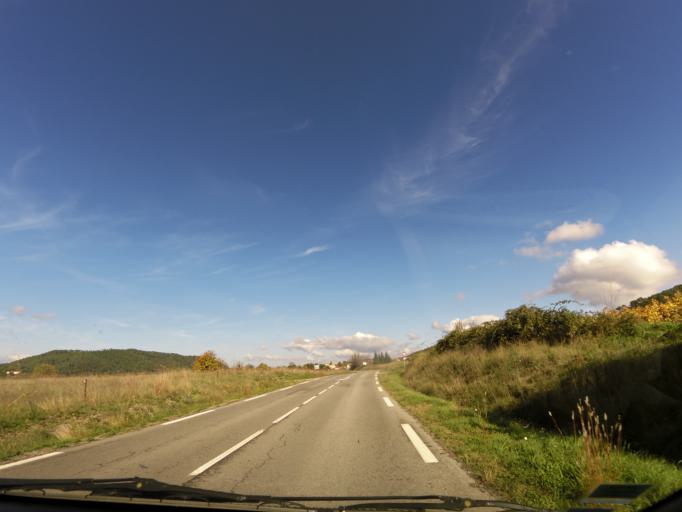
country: FR
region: Languedoc-Roussillon
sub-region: Departement du Gard
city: Saint-Mamert-du-Gard
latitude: 43.8920
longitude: 4.0993
